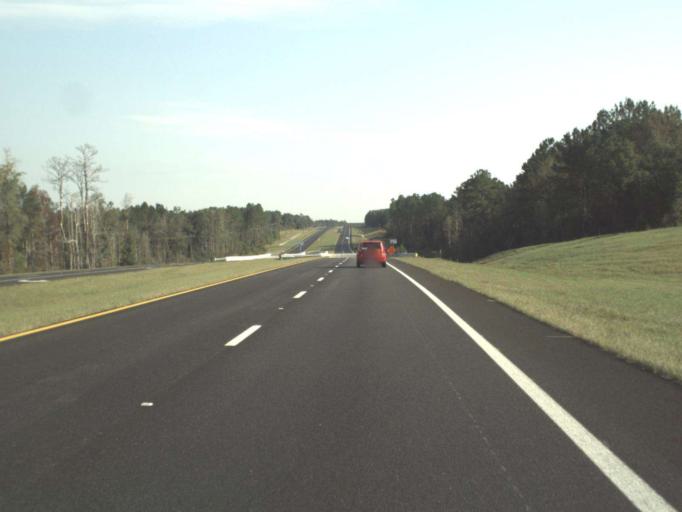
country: US
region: Florida
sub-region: Walton County
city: Freeport
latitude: 30.5261
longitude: -85.8390
